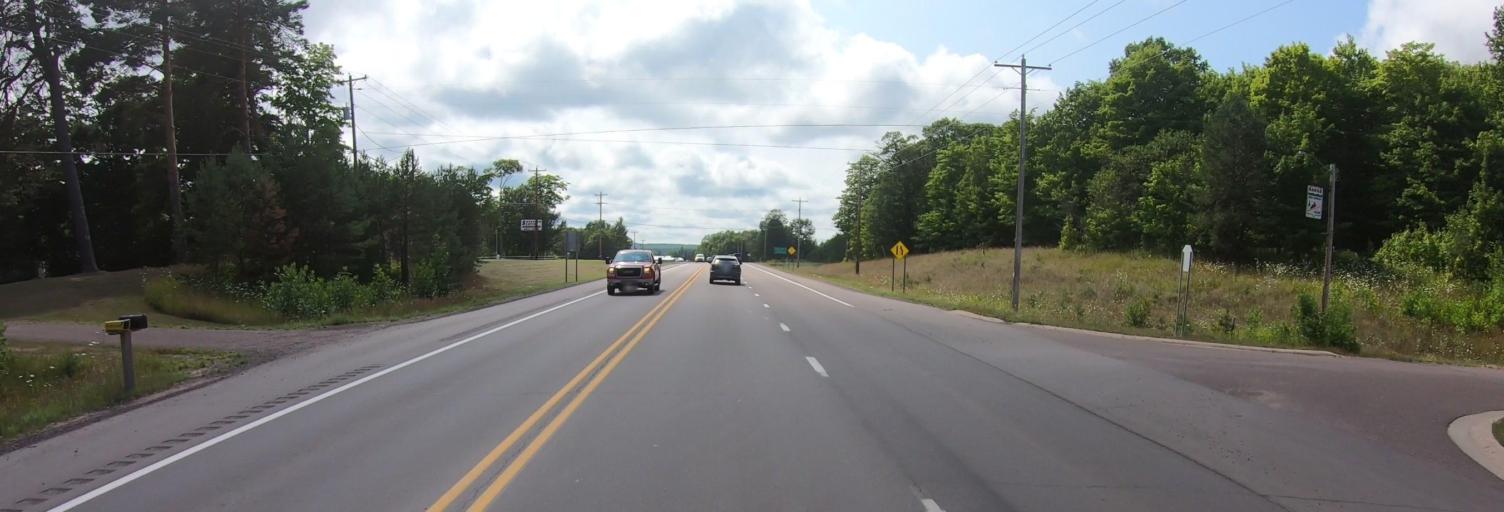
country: US
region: Michigan
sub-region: Houghton County
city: Hancock
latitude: 47.0995
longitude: -88.6111
